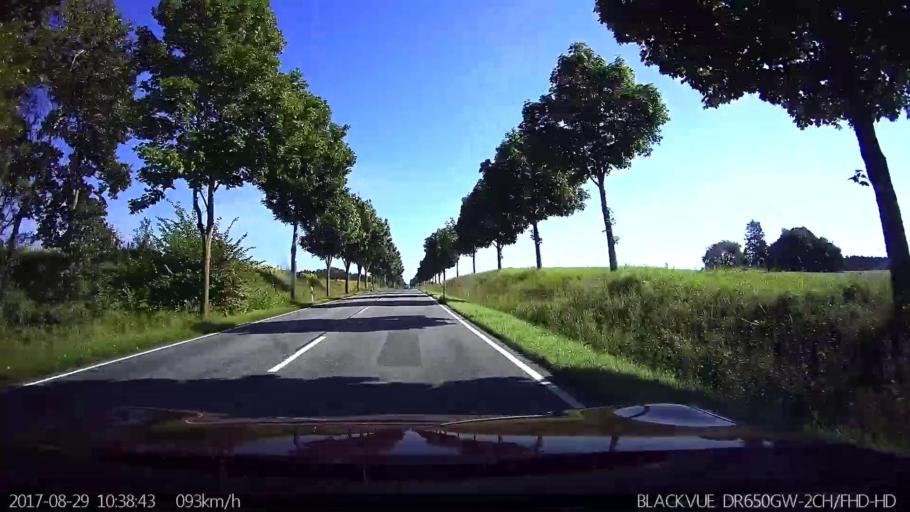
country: DE
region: Mecklenburg-Vorpommern
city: Franzburg
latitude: 54.1686
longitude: 12.8211
